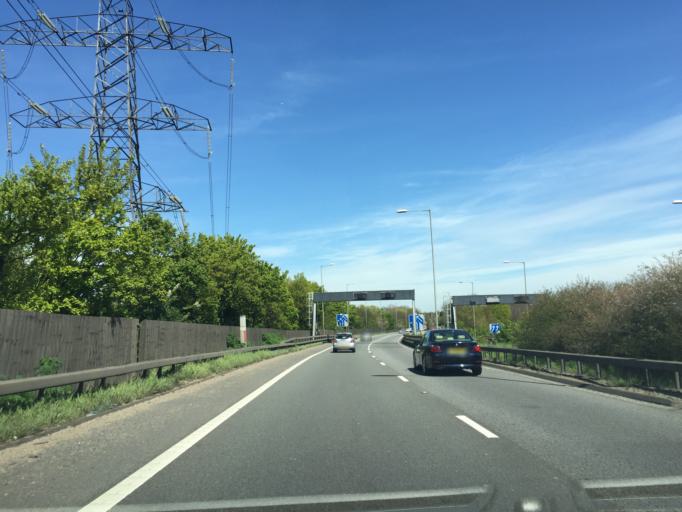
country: GB
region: England
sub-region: Greater London
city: Woodford Green
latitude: 51.5961
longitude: 0.0402
